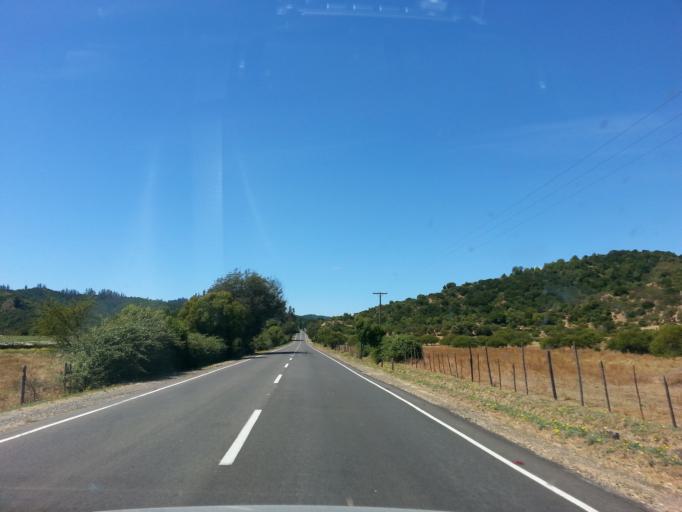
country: CL
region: Valparaiso
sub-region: Provincia de Marga Marga
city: Villa Alemana
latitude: -33.2189
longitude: -71.3909
